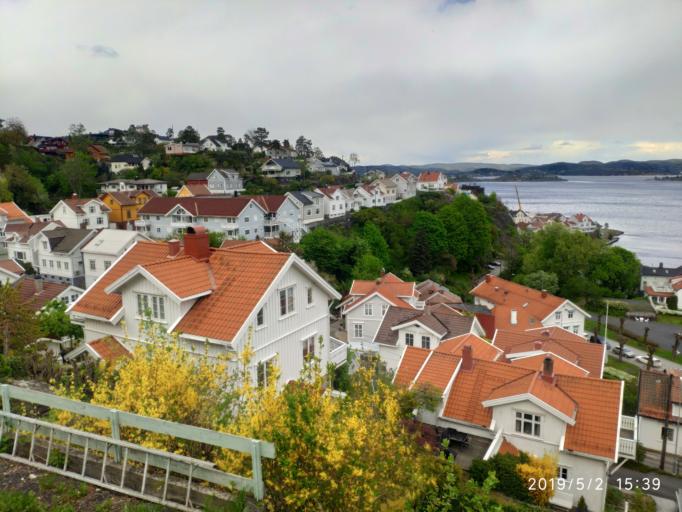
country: NO
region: Telemark
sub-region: Kragero
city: Kragero
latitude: 58.8720
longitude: 9.4114
